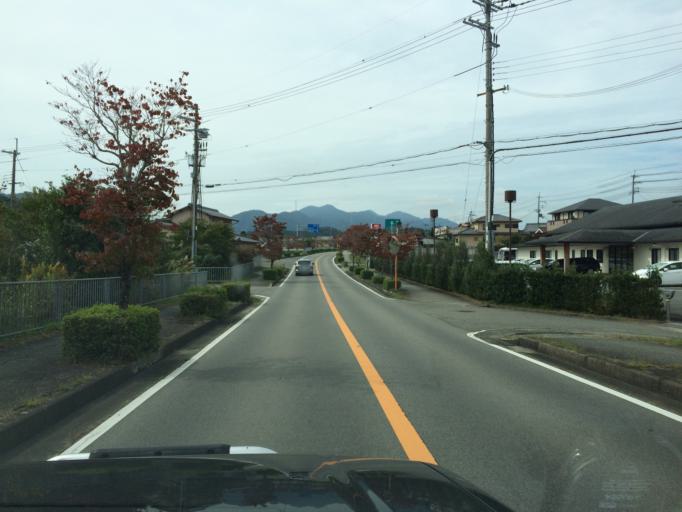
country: JP
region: Hyogo
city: Sasayama
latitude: 35.0734
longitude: 135.2012
